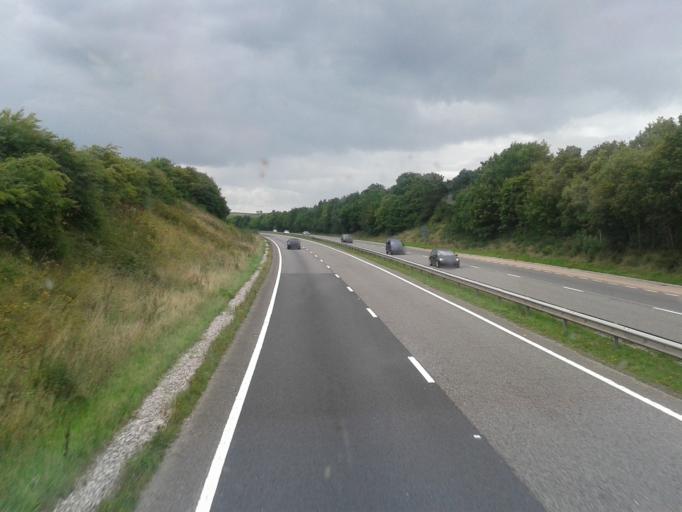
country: GB
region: England
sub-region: Devon
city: Crediton
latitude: 50.7287
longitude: -3.6710
